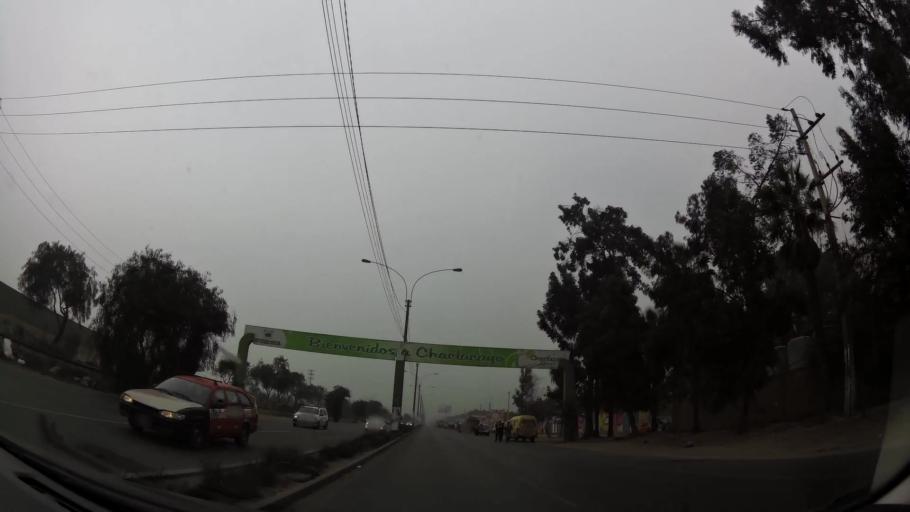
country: PE
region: Lima
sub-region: Lima
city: Santa Maria
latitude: -11.9947
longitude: -76.8314
